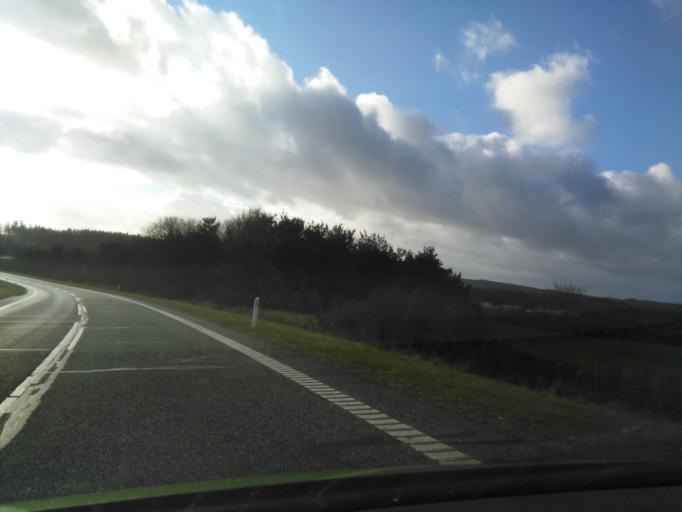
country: DK
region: Central Jutland
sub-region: Skanderborg Kommune
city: Skanderborg
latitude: 56.0188
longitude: 9.8847
